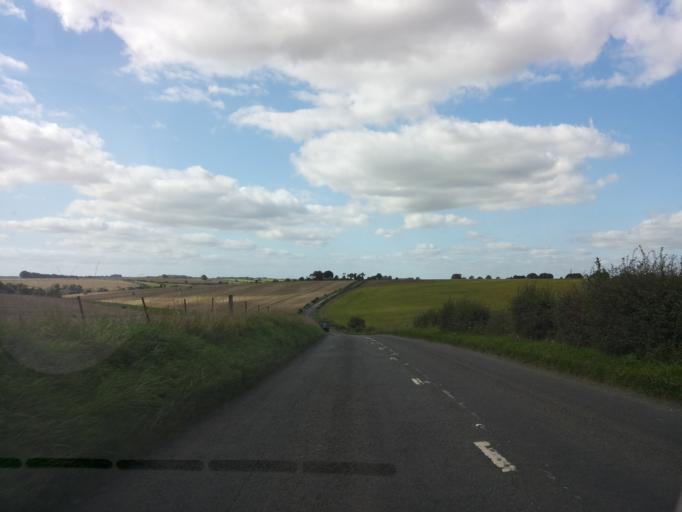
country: GB
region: England
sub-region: Wiltshire
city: Shrewton
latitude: 51.1864
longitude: -1.8725
